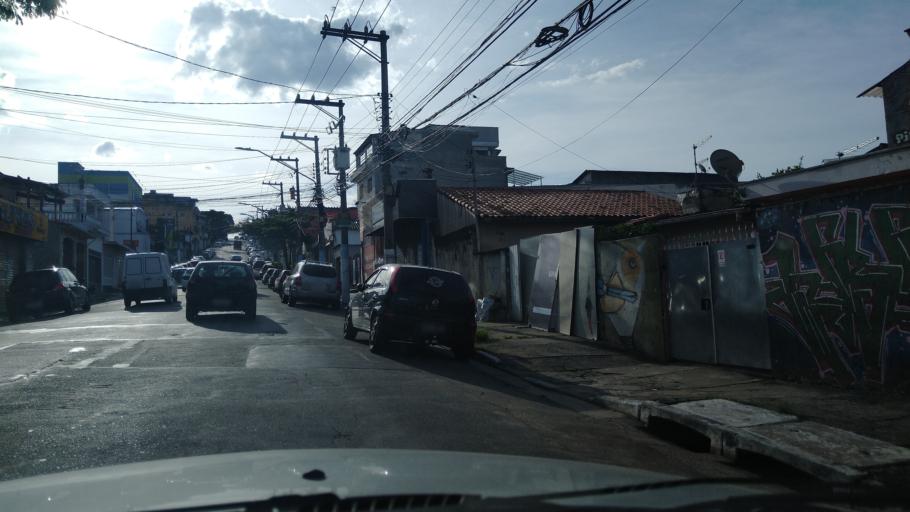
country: BR
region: Sao Paulo
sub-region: Osasco
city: Osasco
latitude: -23.5319
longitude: -46.8028
